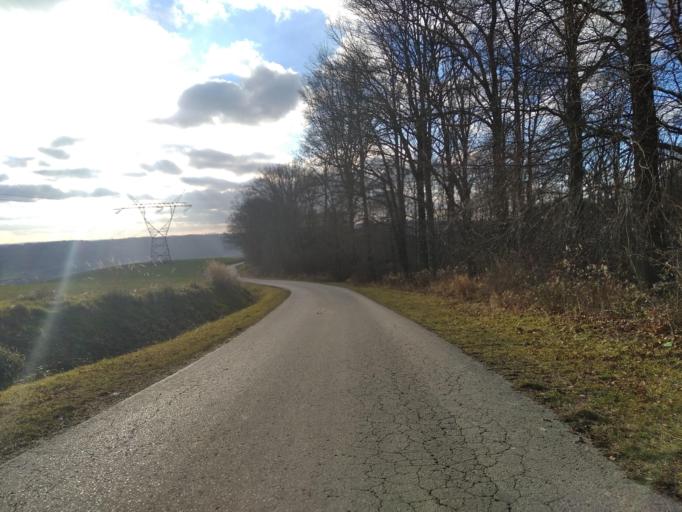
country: PL
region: Subcarpathian Voivodeship
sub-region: Powiat strzyzowski
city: Babica
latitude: 49.9443
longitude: 21.8701
